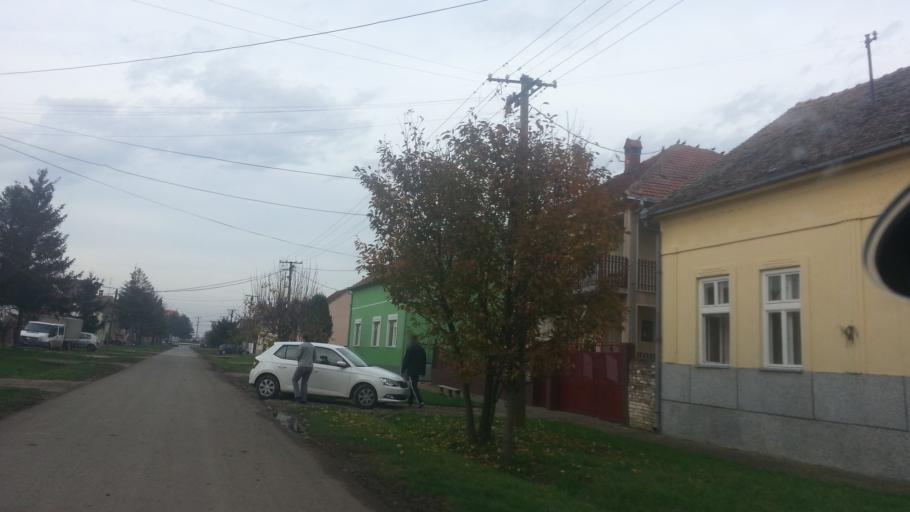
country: RS
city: Putinci
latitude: 44.9639
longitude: 19.9746
